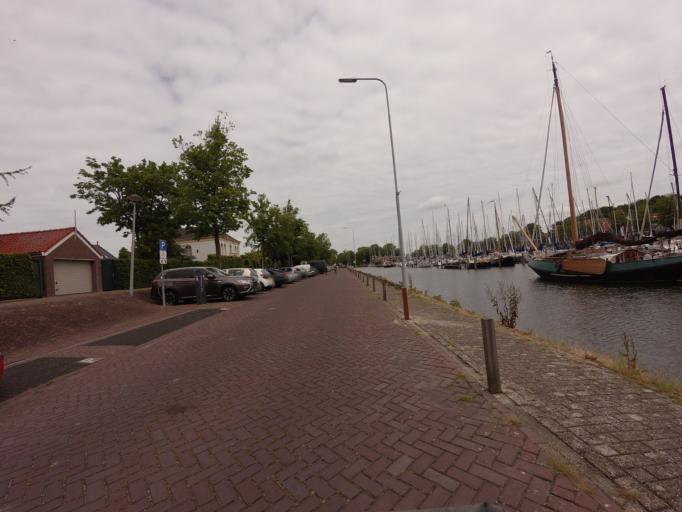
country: NL
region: North Holland
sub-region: Gemeente Medemblik
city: Medemblik
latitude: 52.7702
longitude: 5.1091
